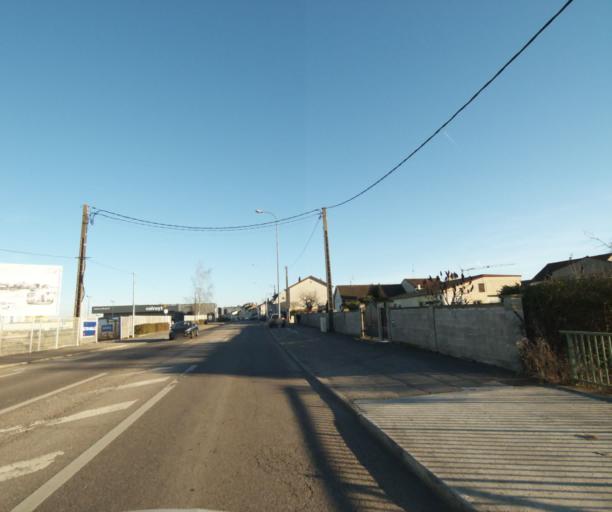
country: FR
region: Lorraine
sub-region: Departement de Meurthe-et-Moselle
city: Laneuveville-devant-Nancy
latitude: 48.6620
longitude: 6.2214
